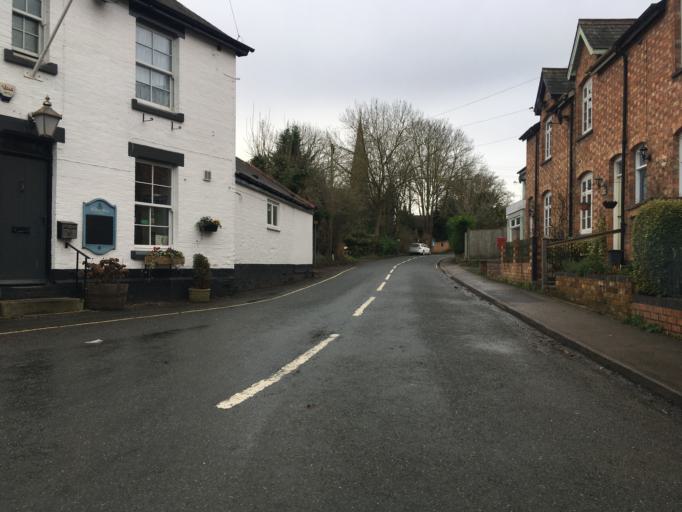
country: GB
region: England
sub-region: Worcestershire
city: Evesham
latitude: 52.0460
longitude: -1.9648
